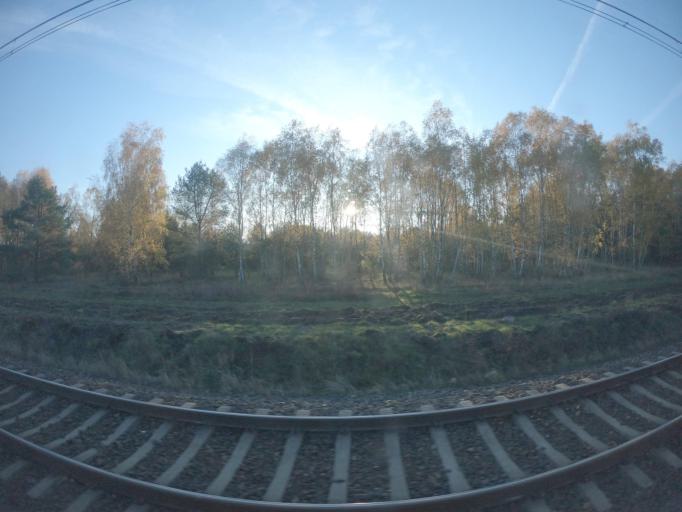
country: PL
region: Lubusz
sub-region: Powiat slubicki
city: Rzepin
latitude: 52.2813
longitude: 14.9034
